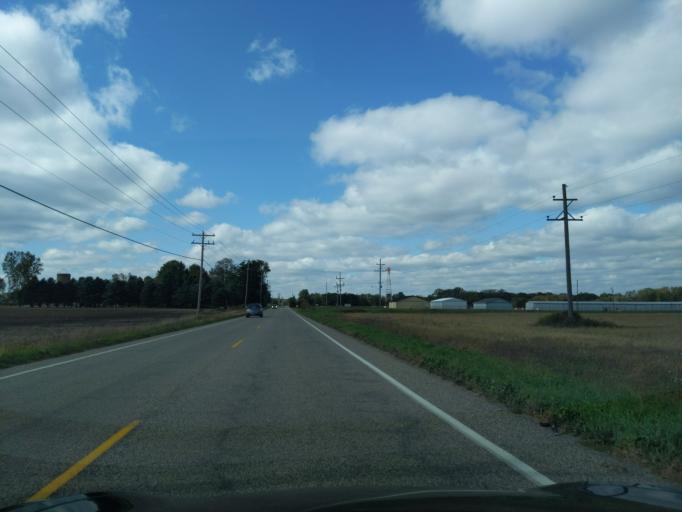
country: US
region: Michigan
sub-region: Eaton County
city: Charlotte
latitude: 42.5676
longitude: -84.8084
